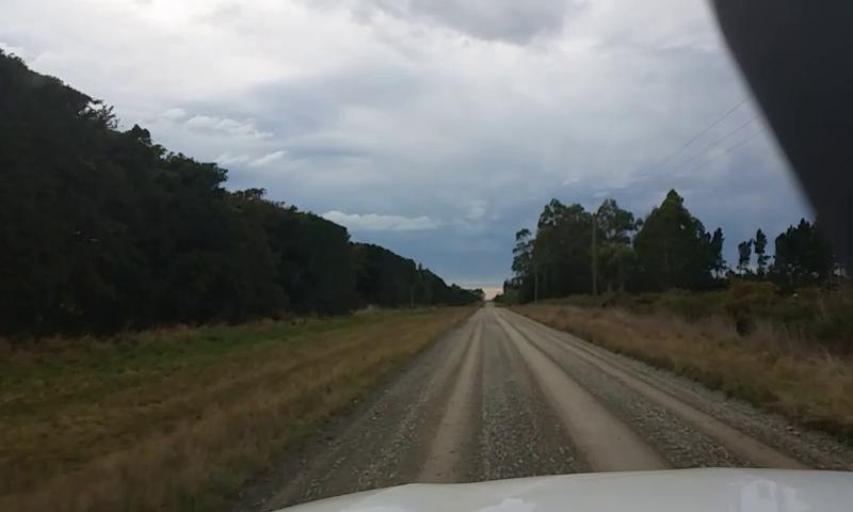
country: NZ
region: Canterbury
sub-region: Waimakariri District
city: Kaiapoi
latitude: -43.2914
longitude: 172.4488
